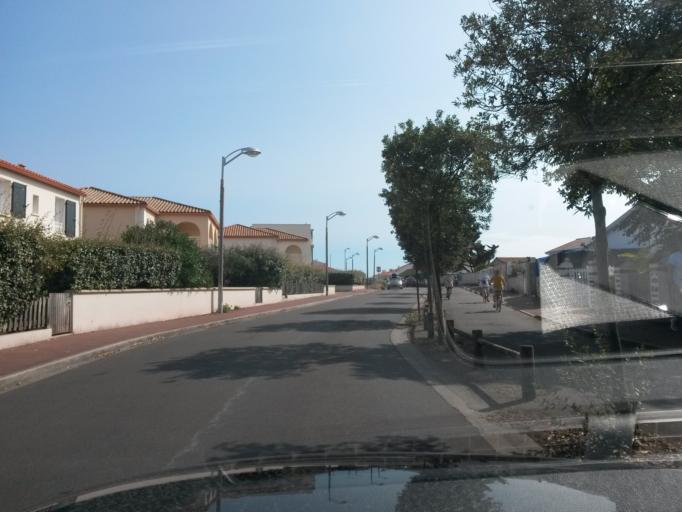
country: FR
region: Pays de la Loire
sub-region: Departement de la Vendee
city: Bretignolles-sur-Mer
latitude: 46.6251
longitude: -1.8736
